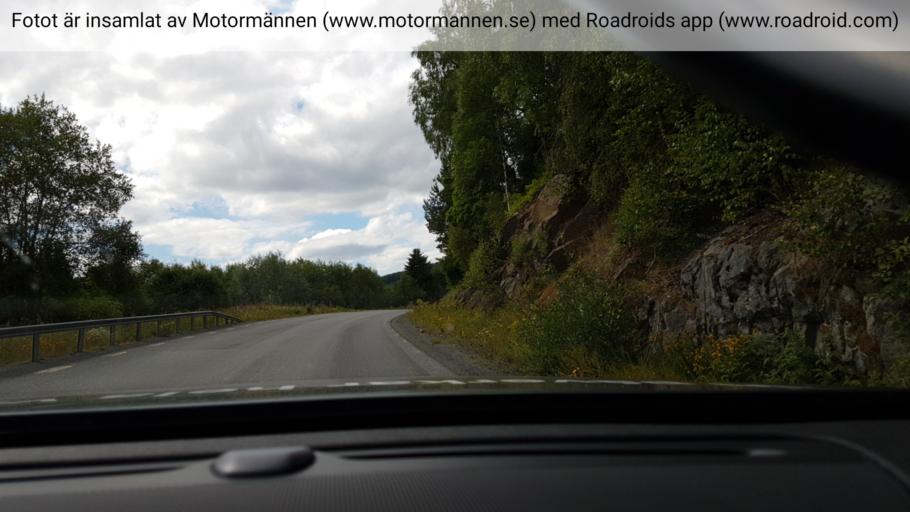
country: SE
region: Vaesternorrland
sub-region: Kramfors Kommun
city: Nordingra
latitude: 62.9403
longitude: 18.2451
